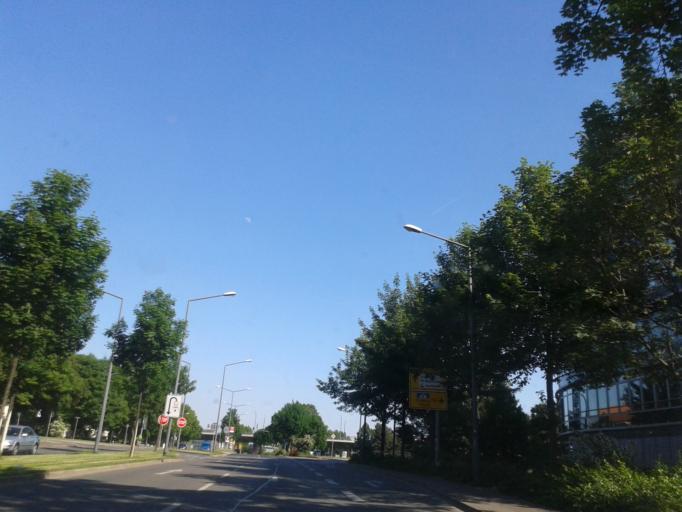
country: DE
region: Saxony
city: Dresden
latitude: 51.0458
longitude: 13.7227
